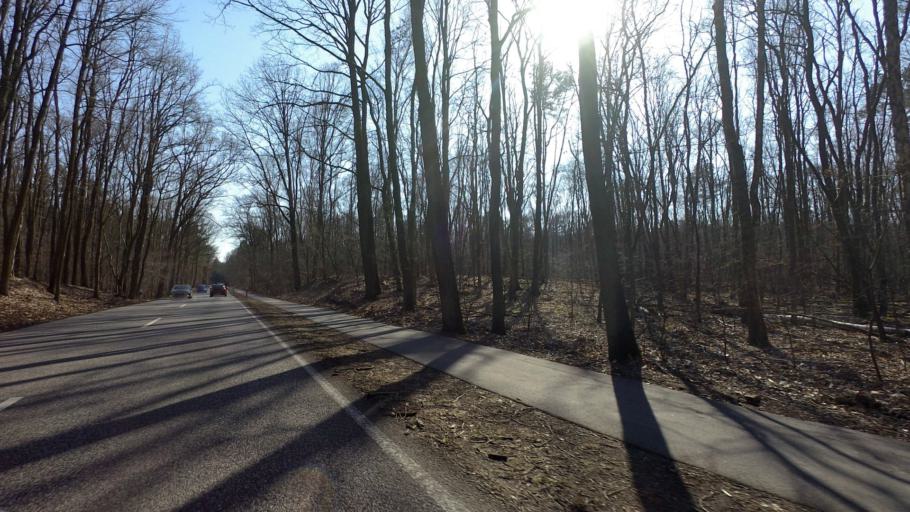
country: DE
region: Berlin
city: Konradshohe
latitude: 52.5921
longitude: 13.2025
